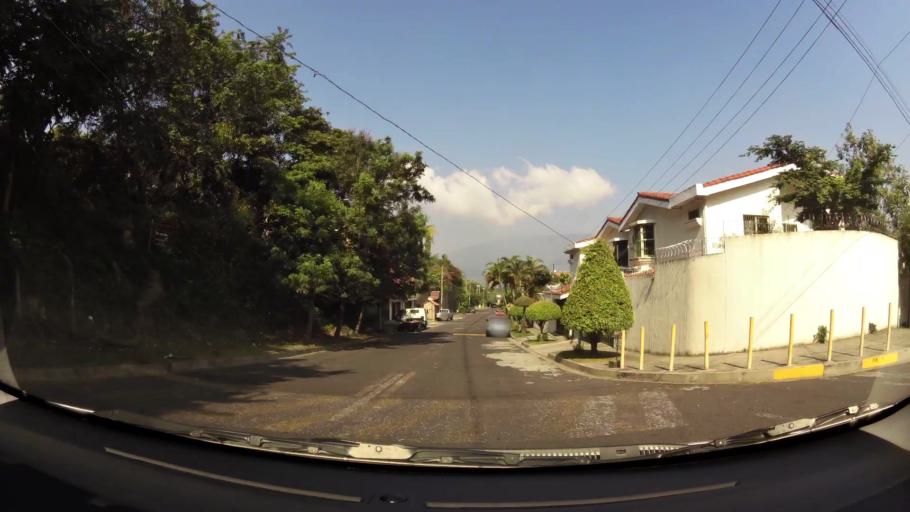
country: SV
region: La Libertad
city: Antiguo Cuscatlan
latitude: 13.6709
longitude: -89.2335
